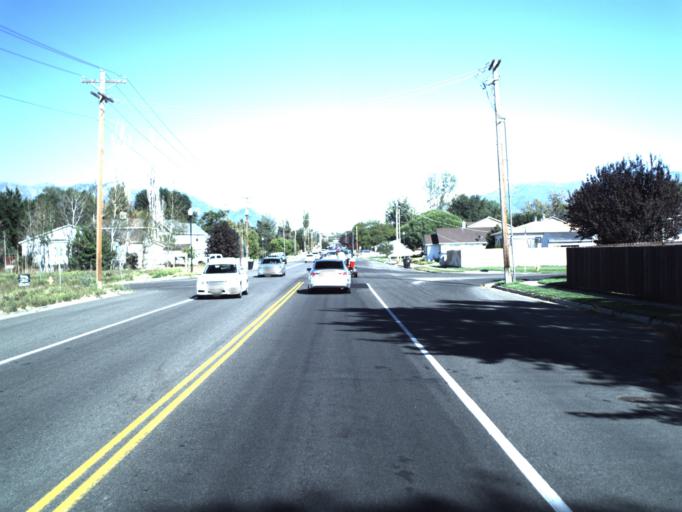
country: US
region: Utah
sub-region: Davis County
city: Clinton
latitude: 41.1399
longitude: -112.0424
